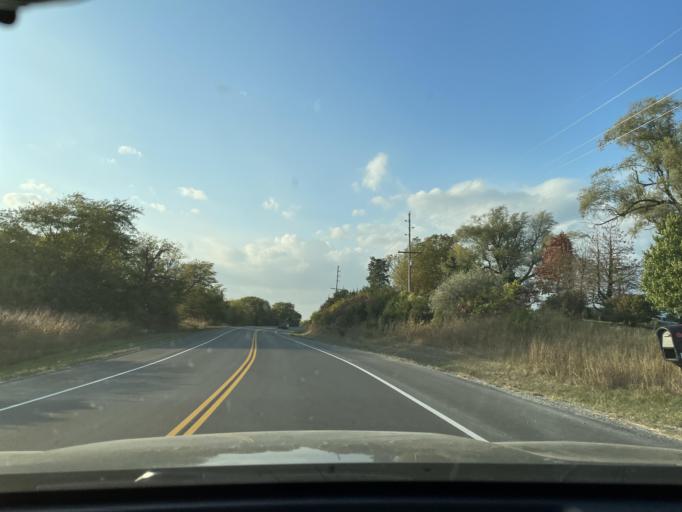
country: US
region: Missouri
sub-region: Andrew County
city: Country Club Village
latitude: 39.8409
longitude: -94.8670
